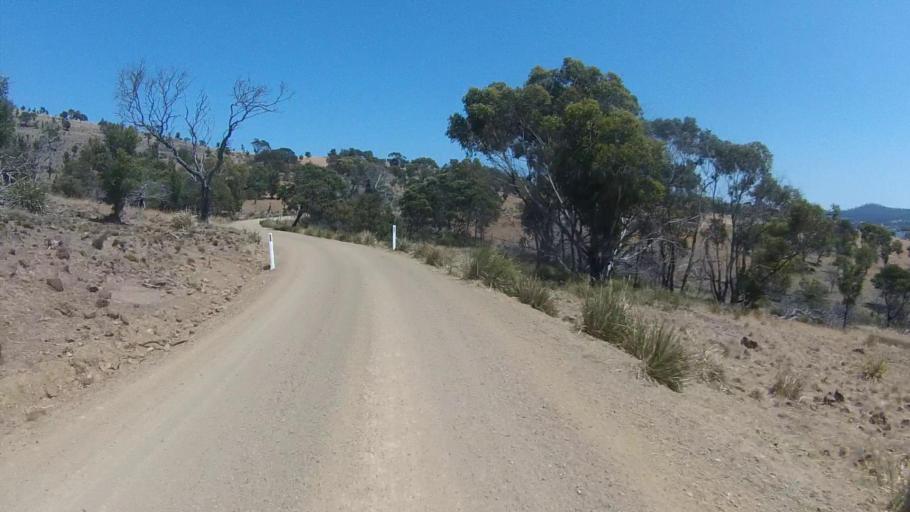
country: AU
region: Tasmania
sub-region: Sorell
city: Sorell
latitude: -42.8921
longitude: 147.8463
